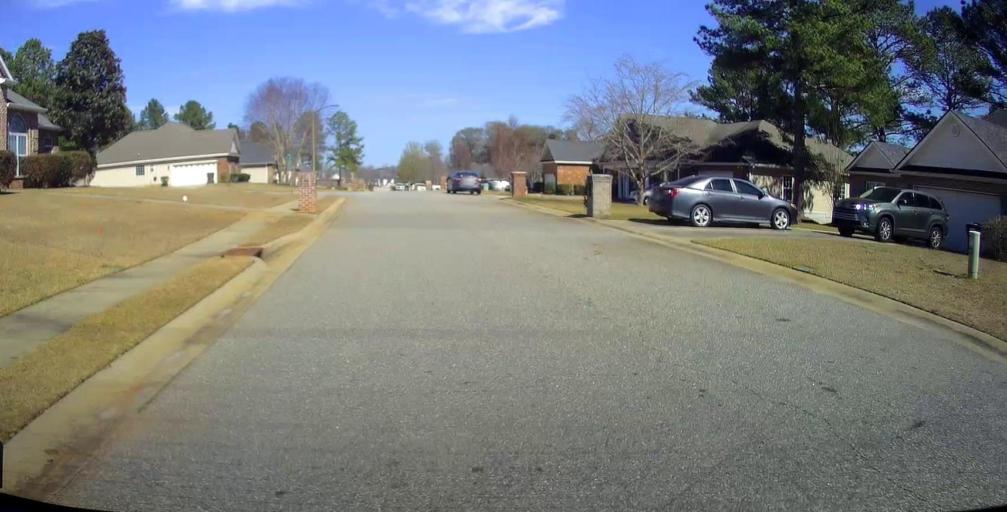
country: US
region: Georgia
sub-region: Houston County
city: Perry
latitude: 32.4989
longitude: -83.6508
